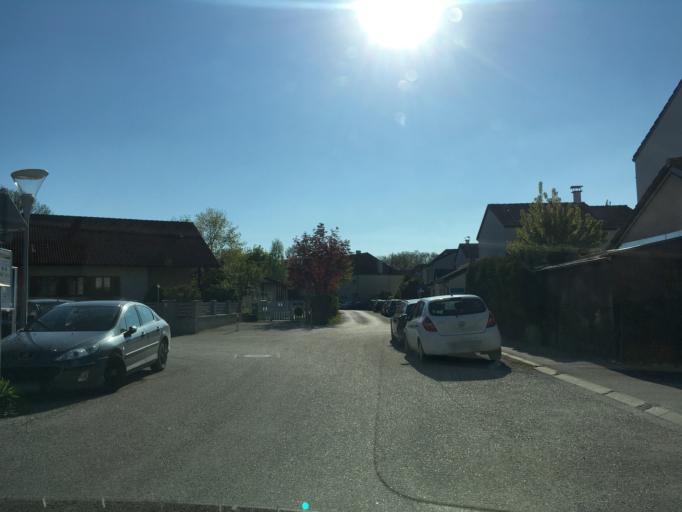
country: AT
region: Lower Austria
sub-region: Politischer Bezirk Ganserndorf
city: Strasshof an der Nordbahn
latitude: 48.3295
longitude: 16.6691
